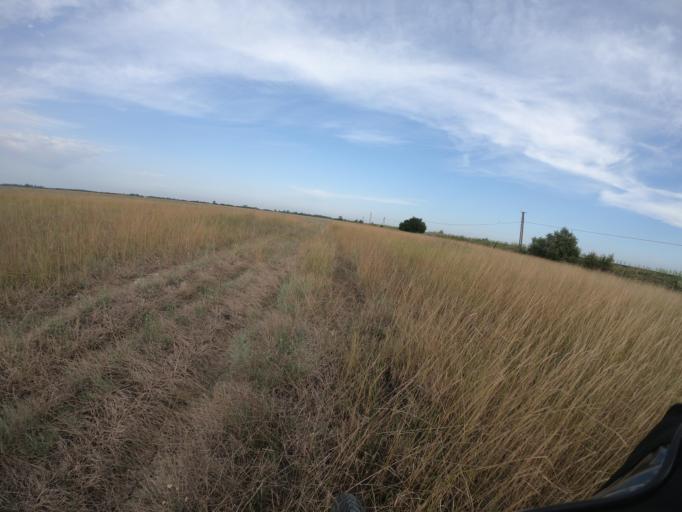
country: HU
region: Hajdu-Bihar
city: Tiszacsege
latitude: 47.6108
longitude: 21.0382
